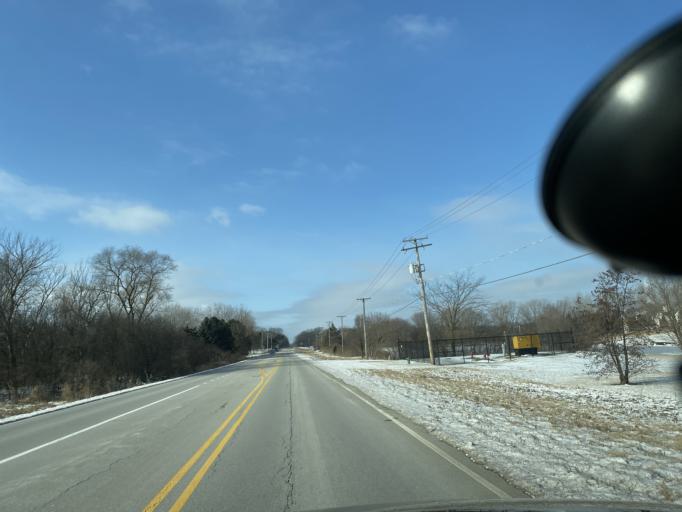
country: US
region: Illinois
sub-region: Will County
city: Goodings Grove
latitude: 41.6503
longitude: -87.9554
